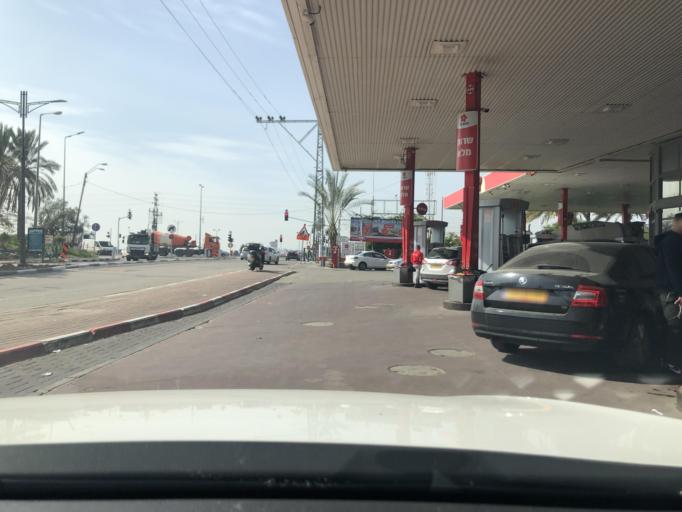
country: IL
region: Central District
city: Rosh Ha'Ayin
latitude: 32.0936
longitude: 34.9413
